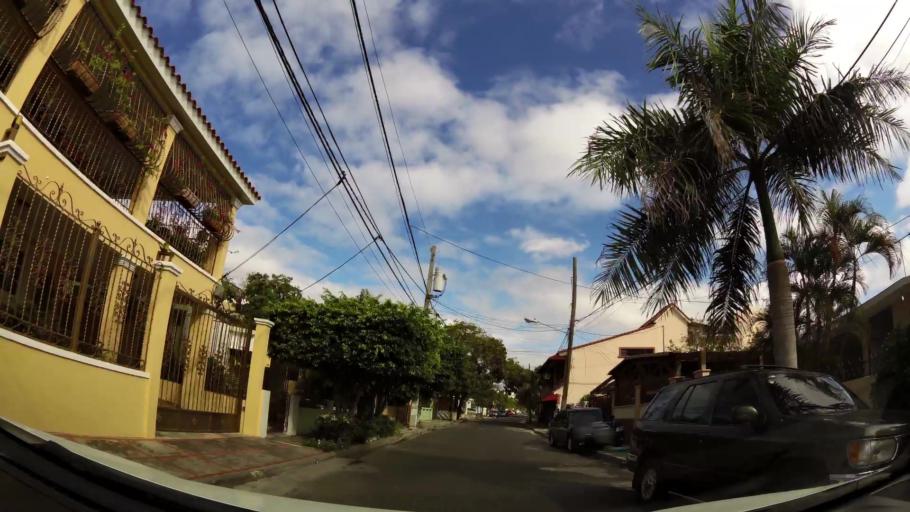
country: DO
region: Nacional
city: Bella Vista
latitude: 18.4445
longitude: -69.9306
